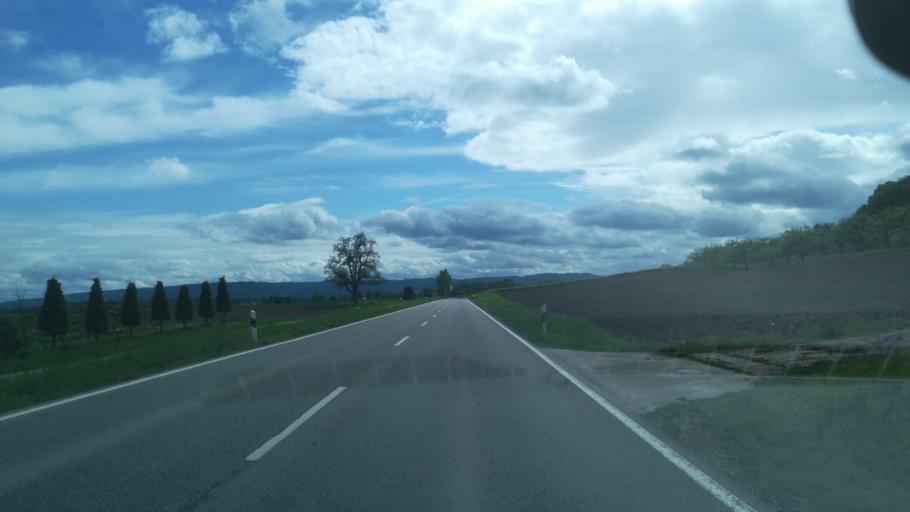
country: DE
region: Baden-Wuerttemberg
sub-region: Freiburg Region
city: Steisslingen
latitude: 47.7910
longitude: 8.9188
